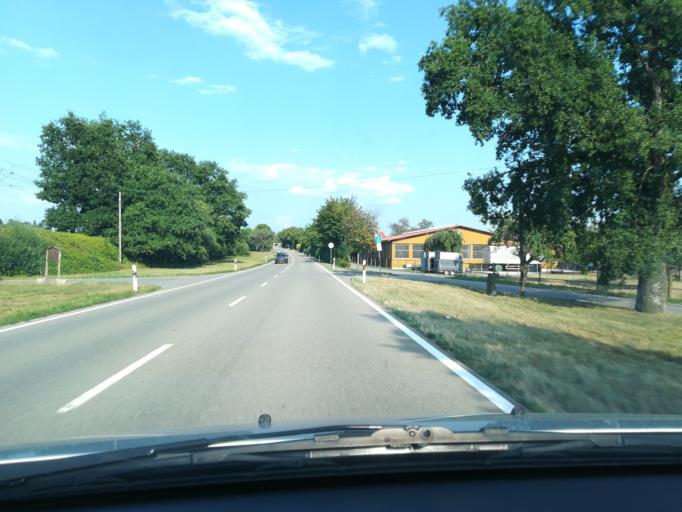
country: DE
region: Baden-Wuerttemberg
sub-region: Freiburg Region
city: Gottmadingen
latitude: 47.7371
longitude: 8.7630
